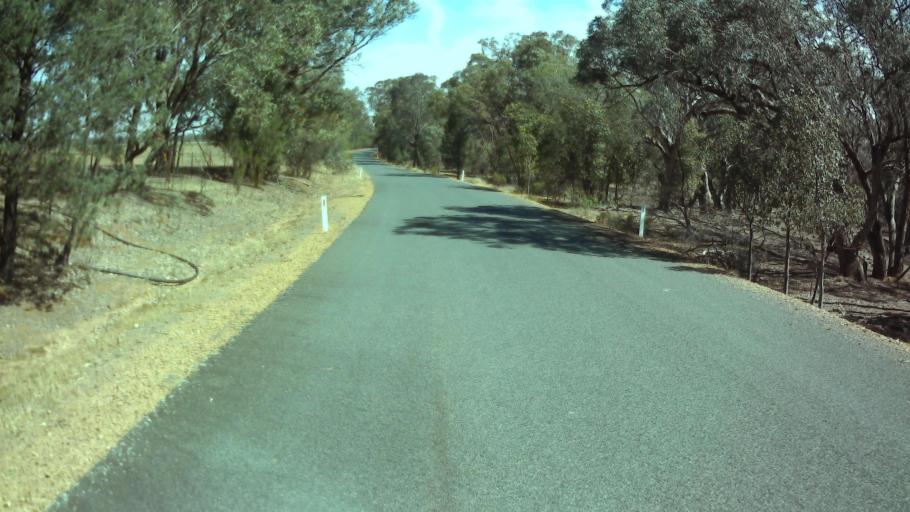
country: AU
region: New South Wales
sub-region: Weddin
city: Grenfell
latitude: -34.0066
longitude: 148.1298
